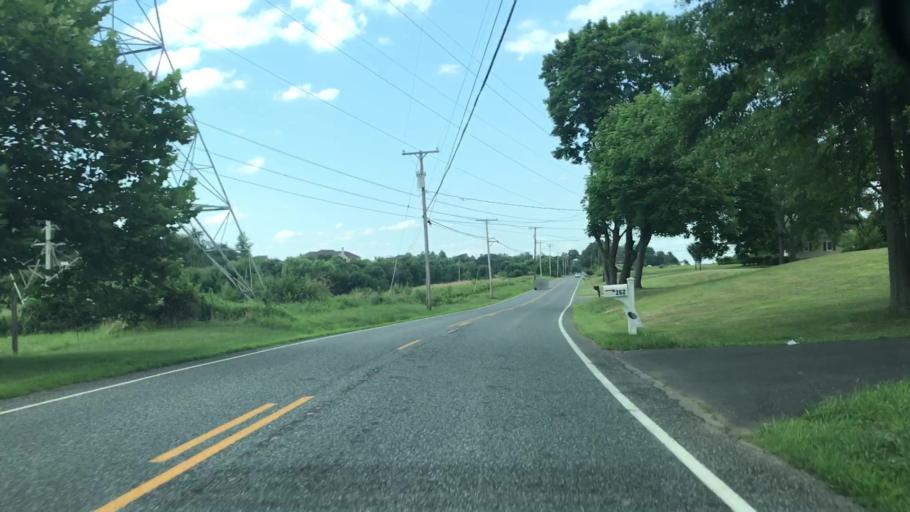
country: US
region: New Jersey
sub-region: Hunterdon County
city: Flemington
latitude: 40.4919
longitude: -74.8118
